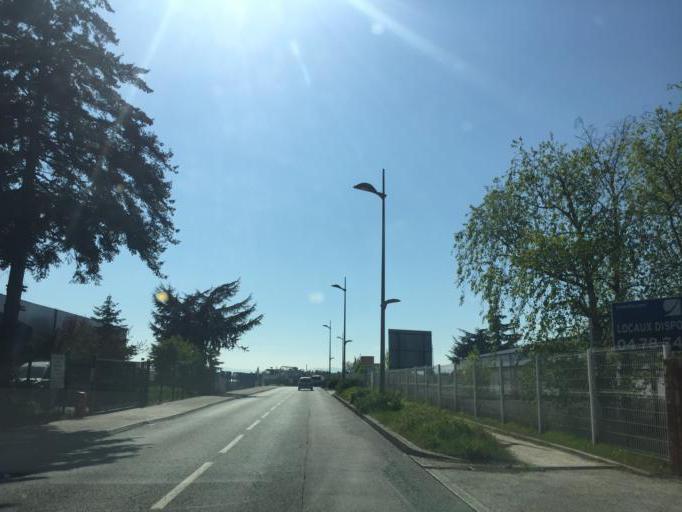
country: FR
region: Rhone-Alpes
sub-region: Departement du Rhone
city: Sathonay-Camp
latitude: 45.8155
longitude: 4.8774
